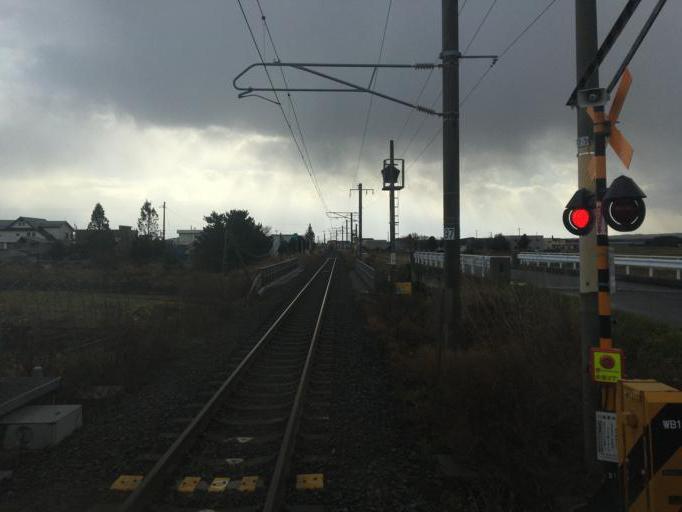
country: JP
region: Aomori
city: Aomori Shi
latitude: 40.8899
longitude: 140.6739
